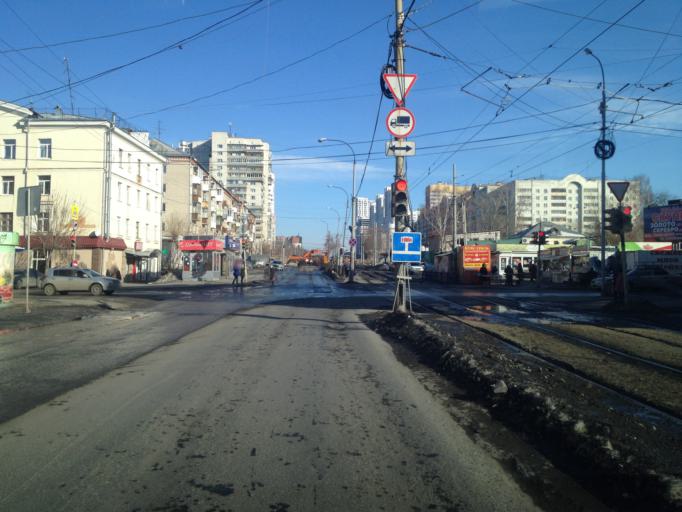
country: RU
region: Sverdlovsk
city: Yekaterinburg
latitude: 56.8360
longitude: 60.5525
